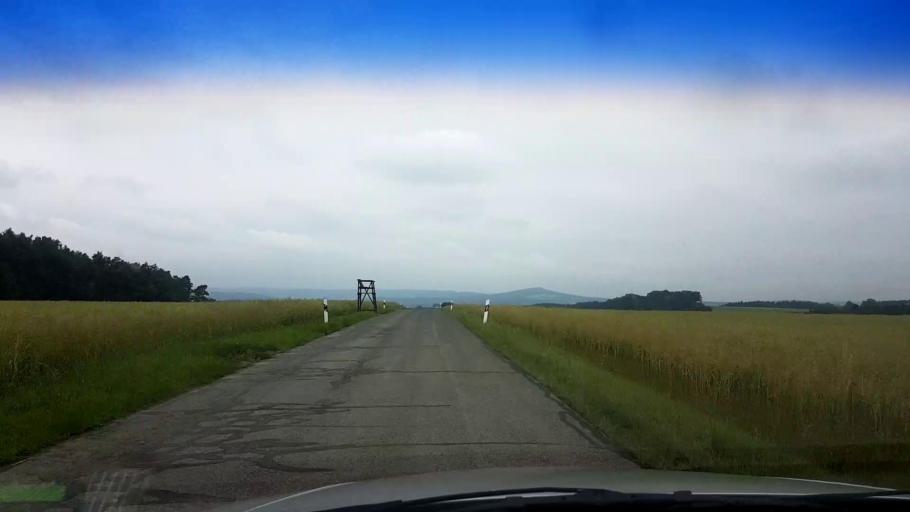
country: DE
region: Bavaria
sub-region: Upper Franconia
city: Kasendorf
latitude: 50.0750
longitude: 11.3371
